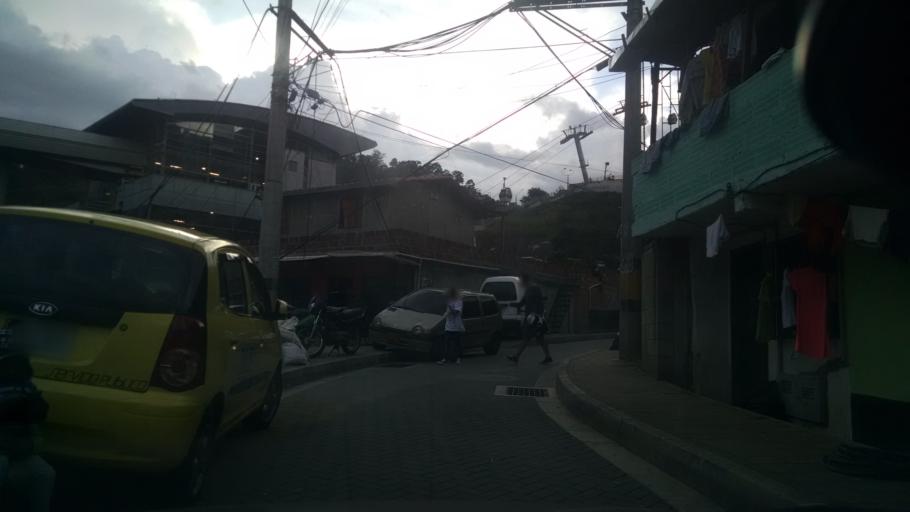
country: CO
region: Antioquia
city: Medellin
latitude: 6.2653
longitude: -75.6129
